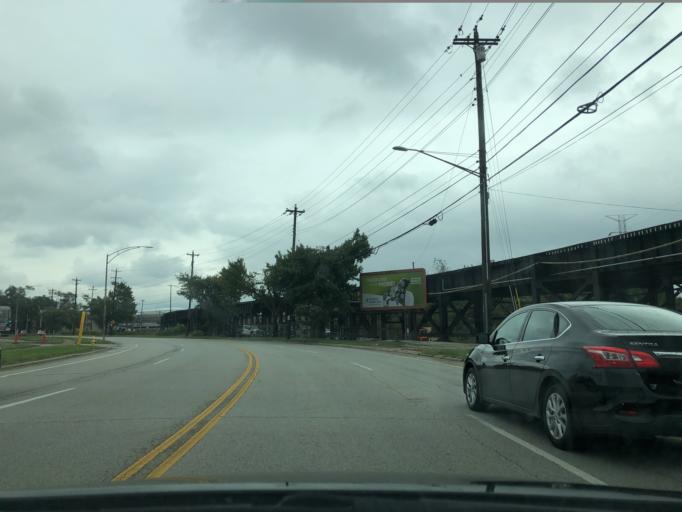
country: US
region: Kentucky
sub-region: Kenton County
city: Ludlow
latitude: 39.0979
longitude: -84.5291
